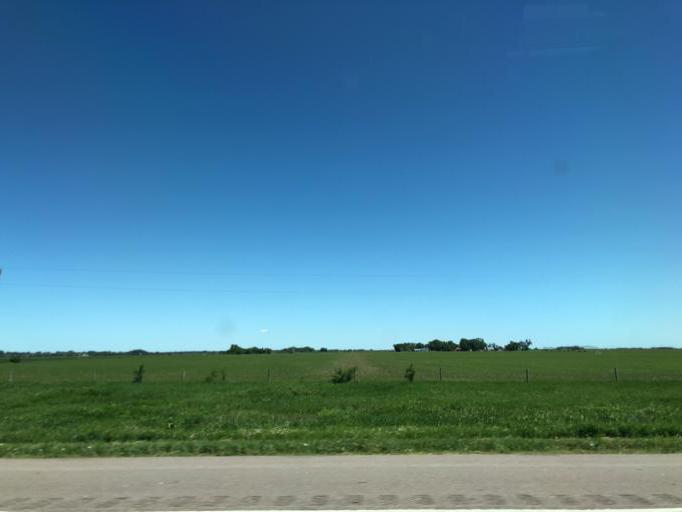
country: US
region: Nebraska
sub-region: York County
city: York
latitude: 40.8222
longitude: -97.5657
